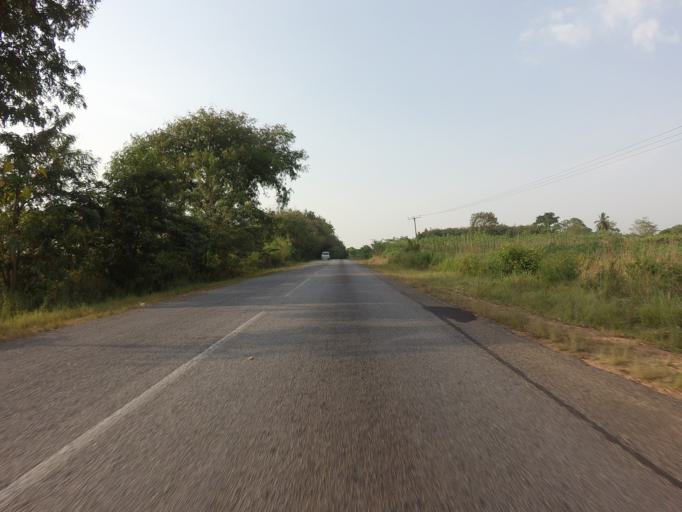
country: GH
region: Volta
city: Ho
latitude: 6.3958
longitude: 0.1798
